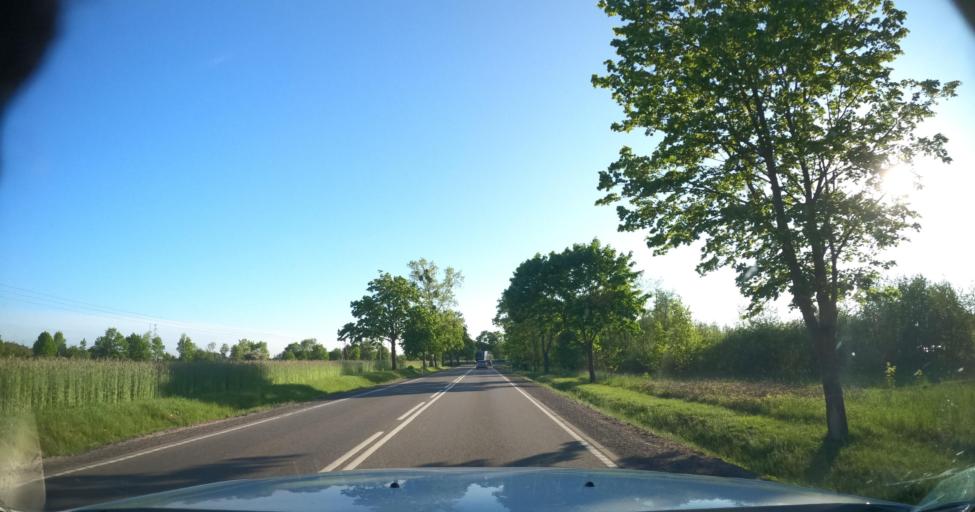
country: PL
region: Pomeranian Voivodeship
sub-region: Powiat kartuski
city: Banino
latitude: 54.3431
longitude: 18.4500
